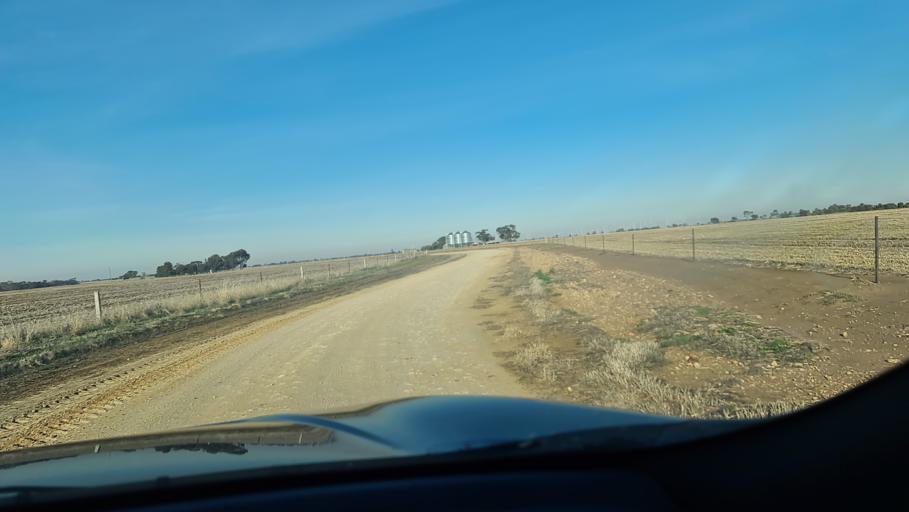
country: AU
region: Victoria
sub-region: Horsham
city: Horsham
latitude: -36.3611
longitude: 142.3966
